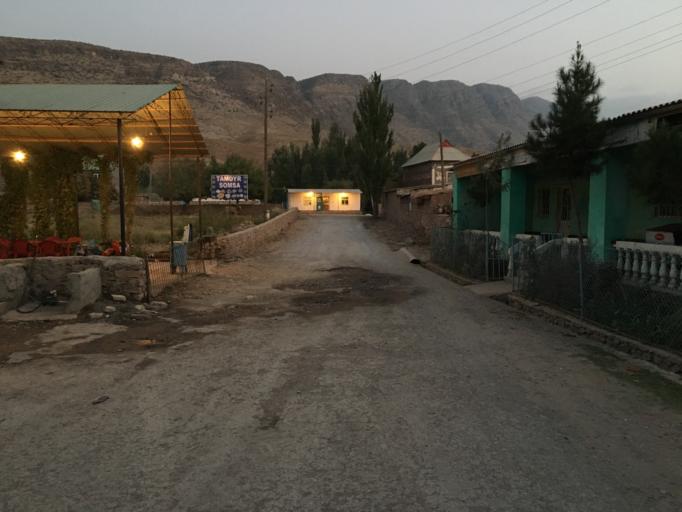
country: UZ
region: Qashqadaryo
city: Qorashina
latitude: 37.9190
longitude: 66.4844
